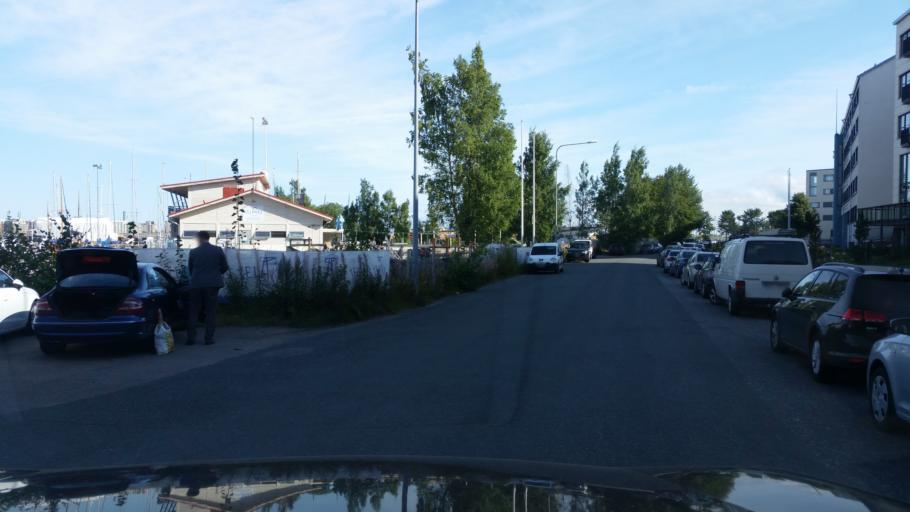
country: FI
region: Uusimaa
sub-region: Helsinki
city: Helsinki
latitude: 60.1593
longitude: 24.8830
